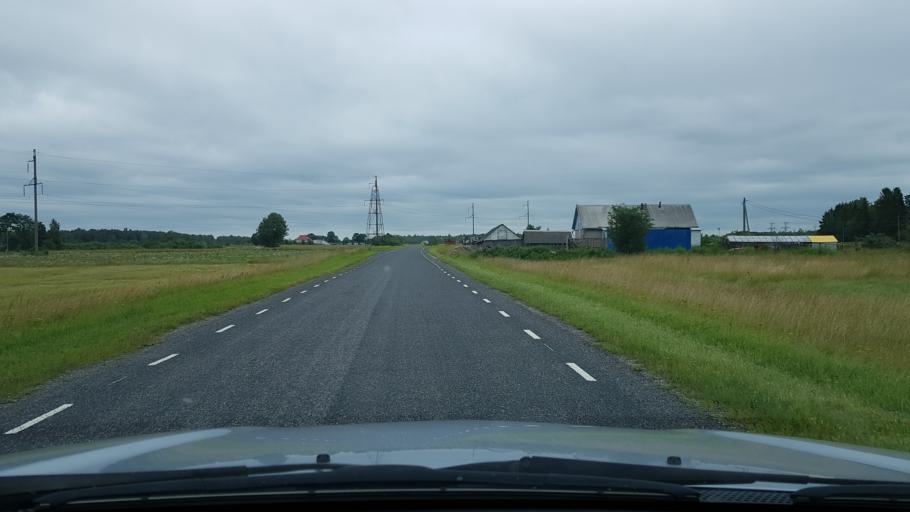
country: EE
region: Ida-Virumaa
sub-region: Narva linn
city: Narva
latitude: 59.3708
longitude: 28.0941
